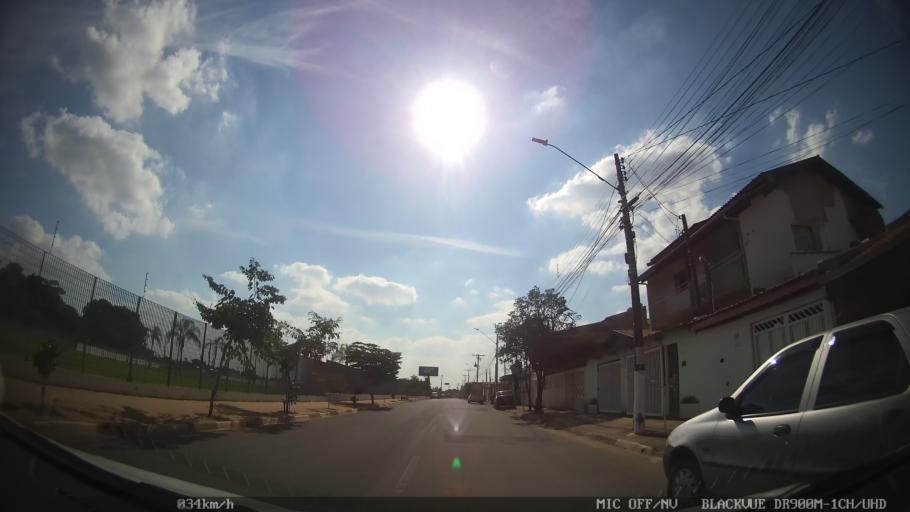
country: BR
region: Sao Paulo
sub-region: Hortolandia
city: Hortolandia
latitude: -22.9016
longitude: -47.2512
